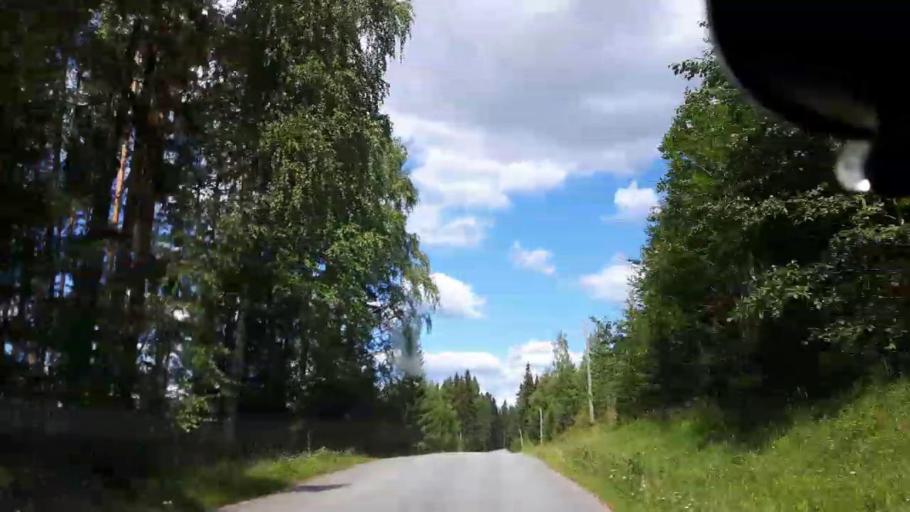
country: SE
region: Jaemtland
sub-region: Ragunda Kommun
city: Hammarstrand
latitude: 62.9367
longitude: 16.6924
